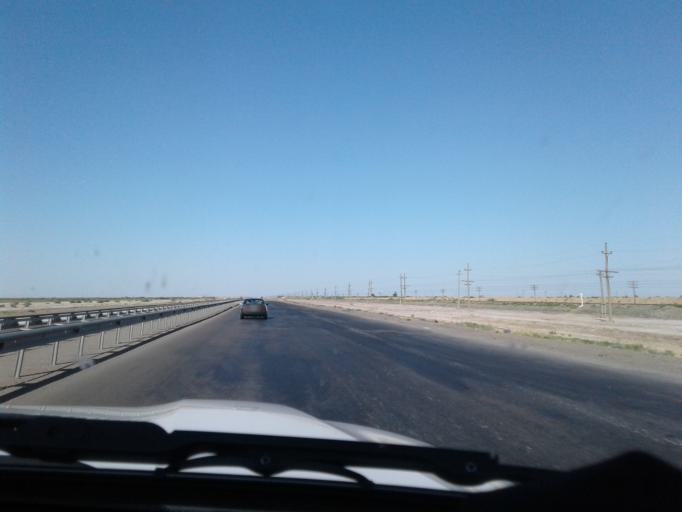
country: IR
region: Razavi Khorasan
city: Kalat-e Naderi
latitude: 37.2185
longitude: 60.1049
